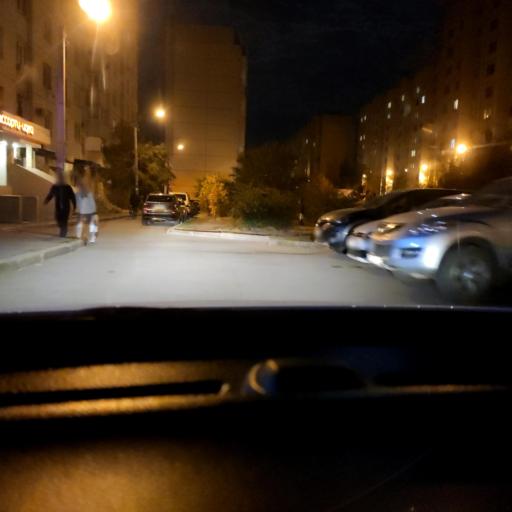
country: RU
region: Voronezj
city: Somovo
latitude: 51.6897
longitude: 39.2819
